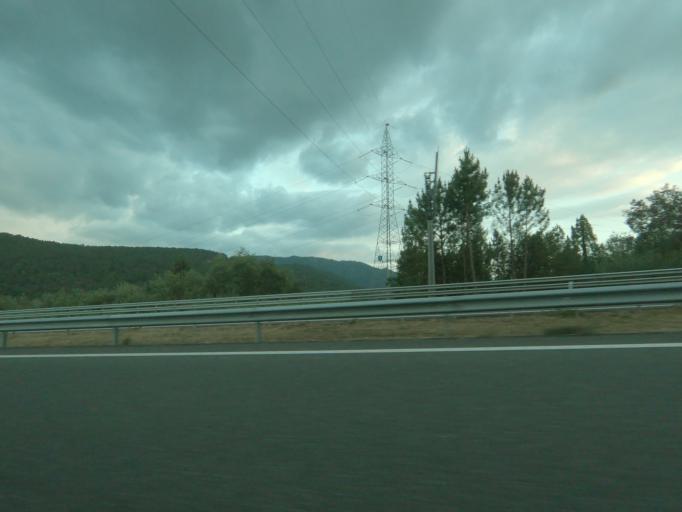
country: ES
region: Galicia
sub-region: Provincia de Ourense
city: Ribadavia
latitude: 42.3017
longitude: -8.1378
